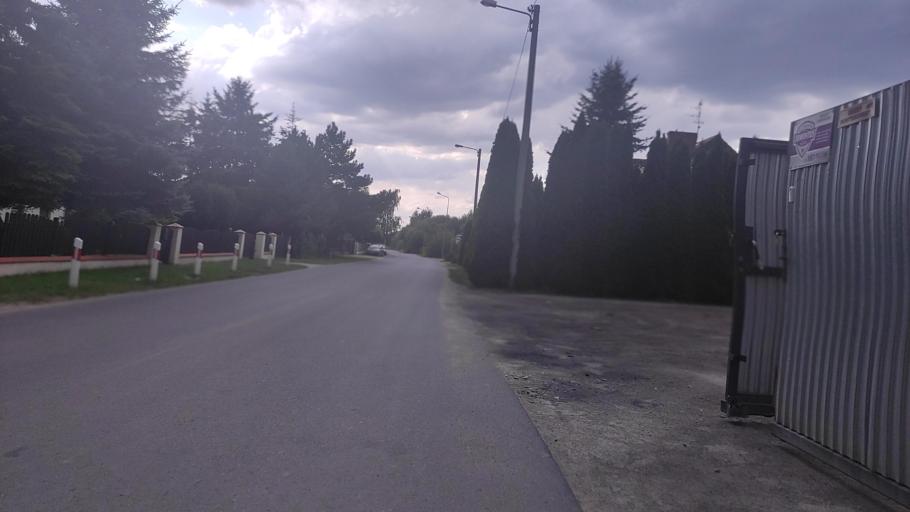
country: PL
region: Greater Poland Voivodeship
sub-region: Powiat poznanski
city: Swarzedz
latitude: 52.3865
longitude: 17.1161
